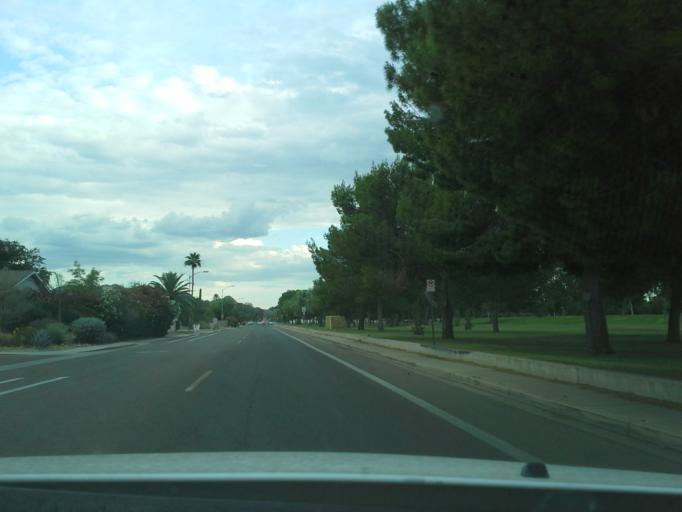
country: US
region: Arizona
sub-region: Maricopa County
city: Paradise Valley
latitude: 33.6007
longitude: -112.0046
